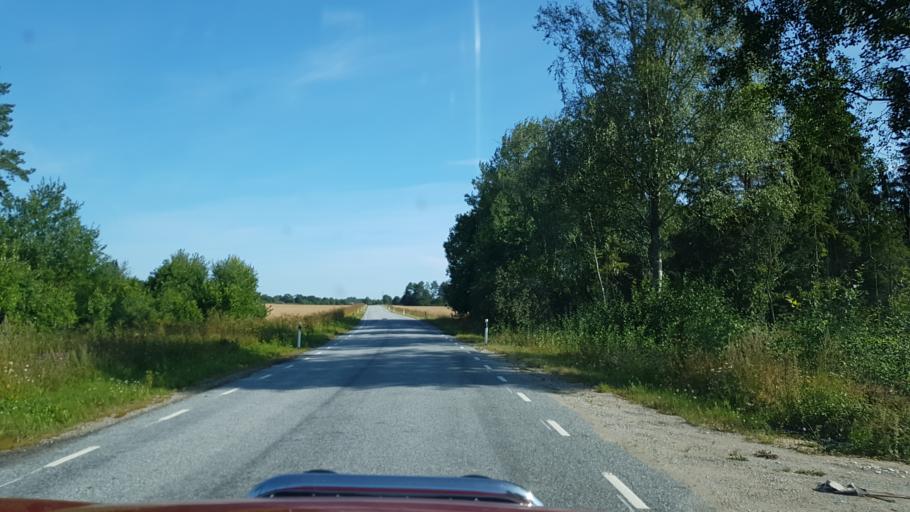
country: EE
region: Harju
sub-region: Raasiku vald
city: Raasiku
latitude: 59.2895
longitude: 25.1677
